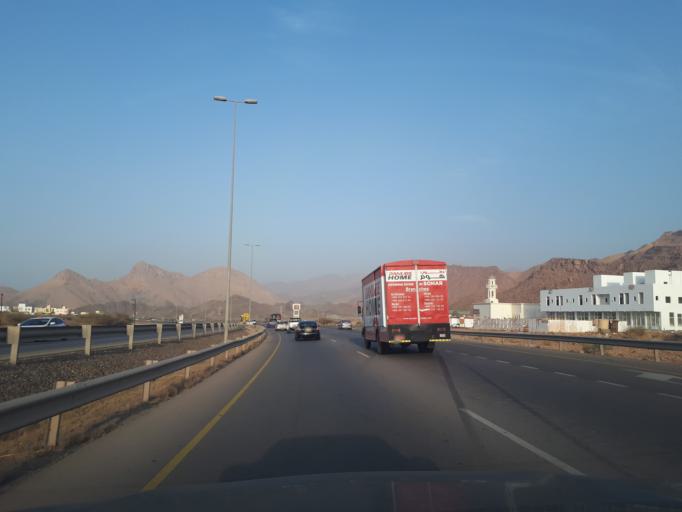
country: OM
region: Muhafazat ad Dakhiliyah
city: Bidbid
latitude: 23.4585
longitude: 58.1704
